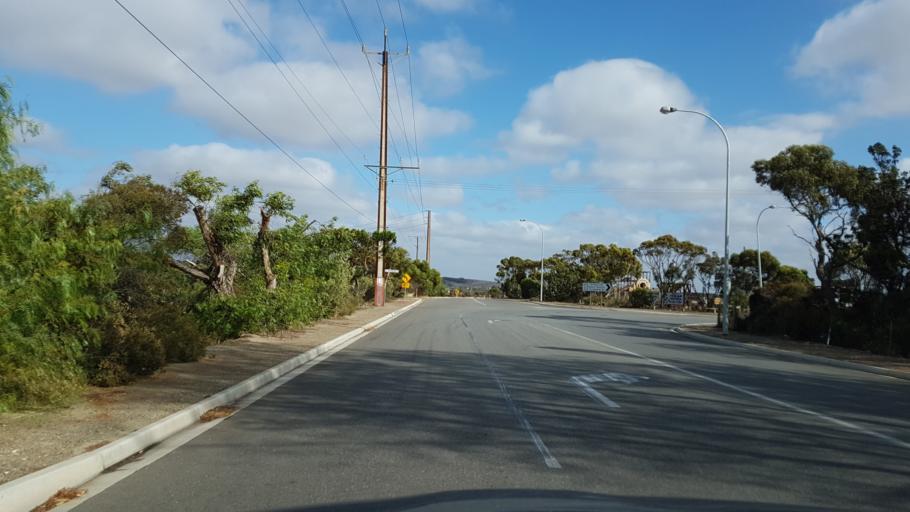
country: AU
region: South Australia
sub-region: Murray Bridge
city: Murray Bridge
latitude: -35.1175
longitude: 139.2473
